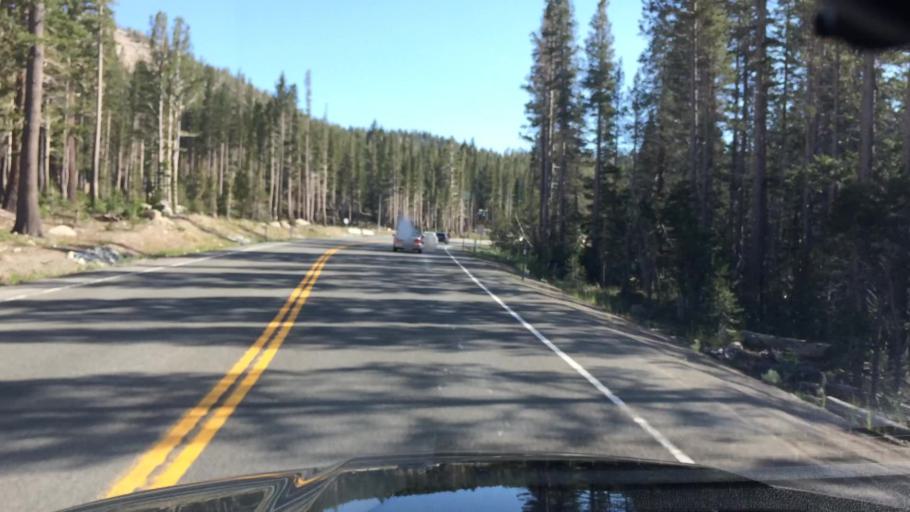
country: US
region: Nevada
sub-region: Washoe County
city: Incline Village
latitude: 39.3254
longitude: -119.8926
